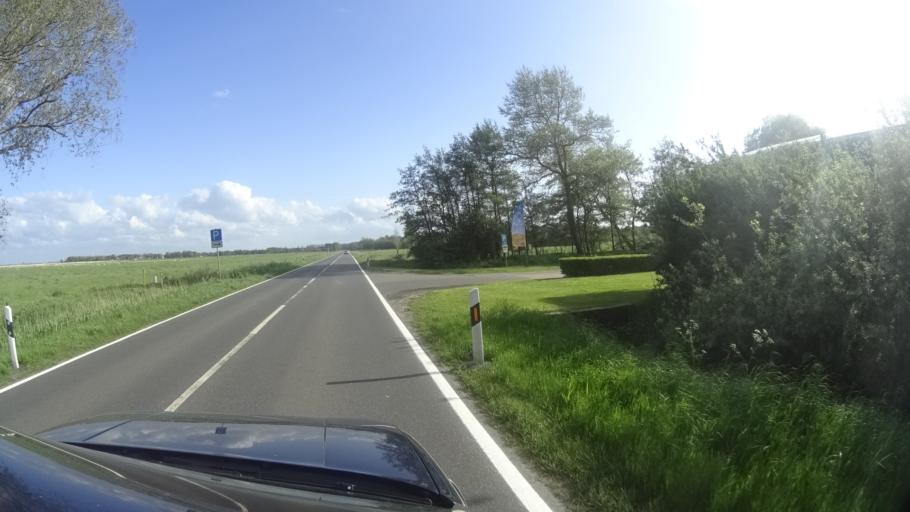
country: DE
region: Mecklenburg-Vorpommern
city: Ostseebad Dierhagen
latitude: 54.3053
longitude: 12.3535
